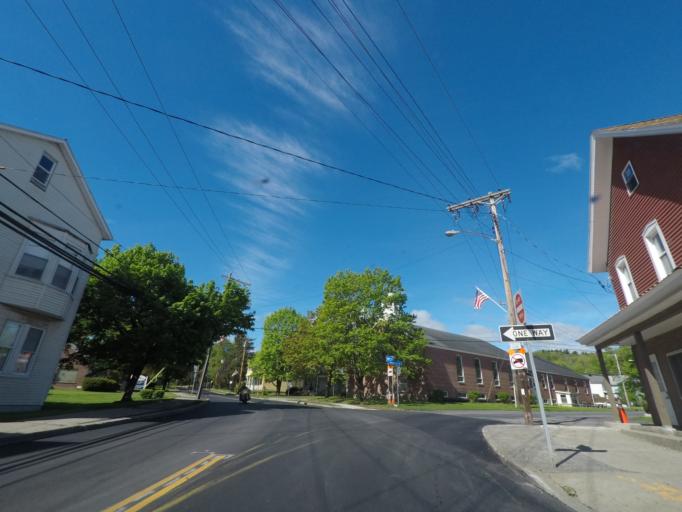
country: US
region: New York
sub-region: Albany County
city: Ravena
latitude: 42.4717
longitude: -73.8130
